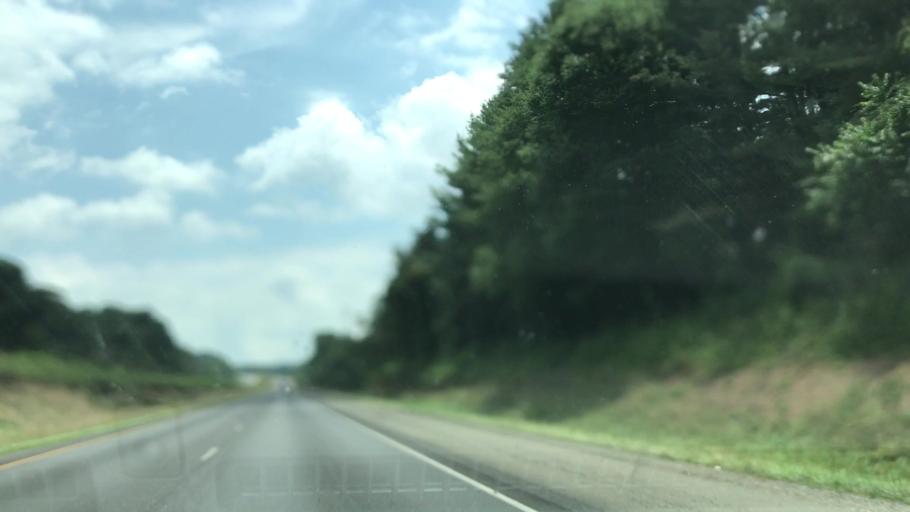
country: US
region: Virginia
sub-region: Carroll County
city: Hillsville
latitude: 36.7109
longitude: -80.7433
